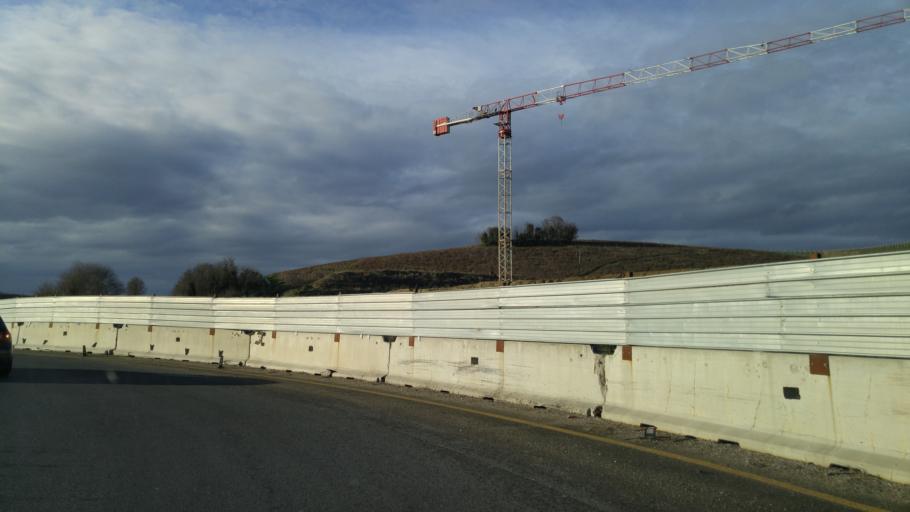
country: IT
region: The Marches
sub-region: Provincia di Ancona
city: Camerano
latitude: 43.5327
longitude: 13.5246
